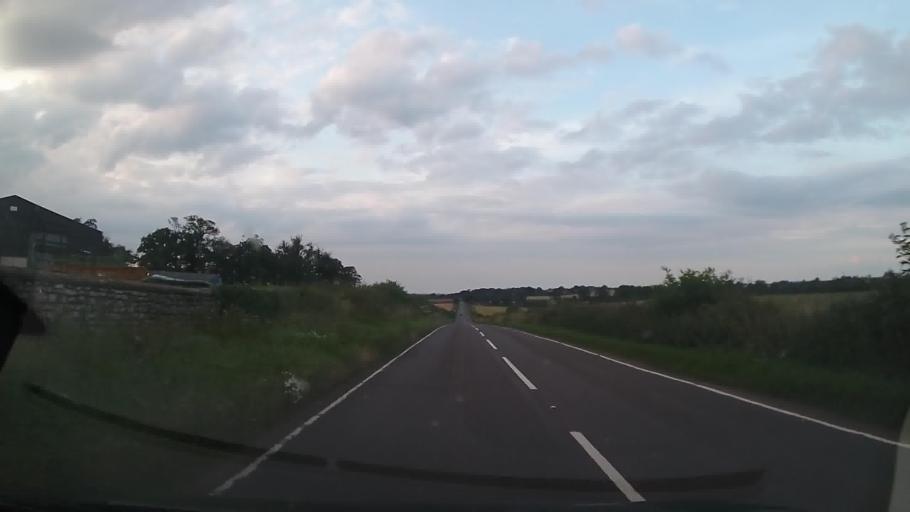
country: GB
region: England
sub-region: Shropshire
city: Clive
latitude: 52.8129
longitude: -2.7461
